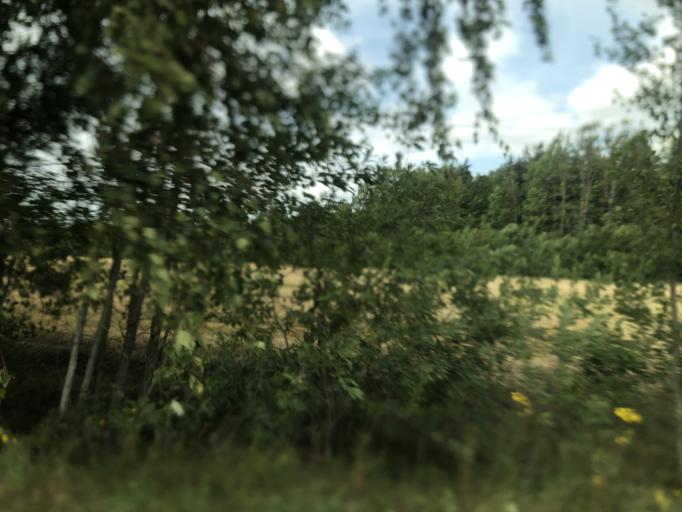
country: LV
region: Vecumnieki
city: Vecumnieki
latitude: 56.4596
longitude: 24.6627
